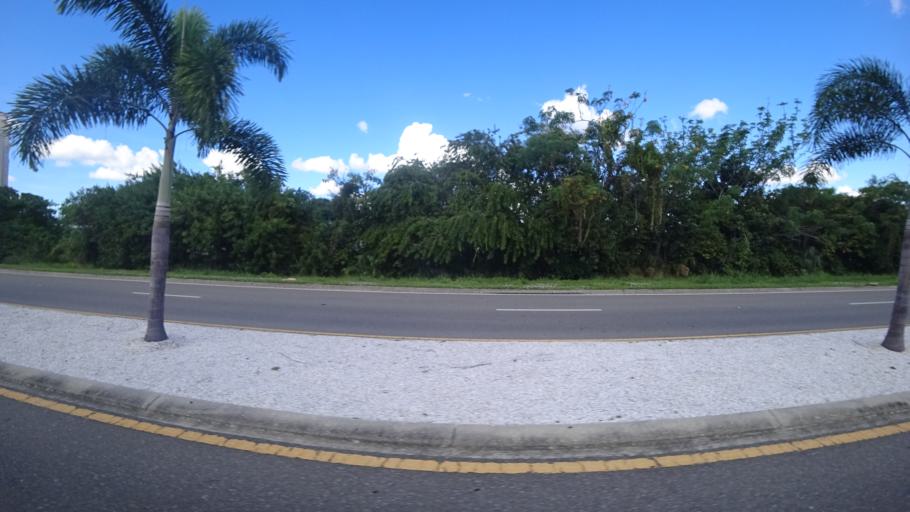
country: US
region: Florida
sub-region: Manatee County
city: Palmetto
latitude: 27.5163
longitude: -82.5556
